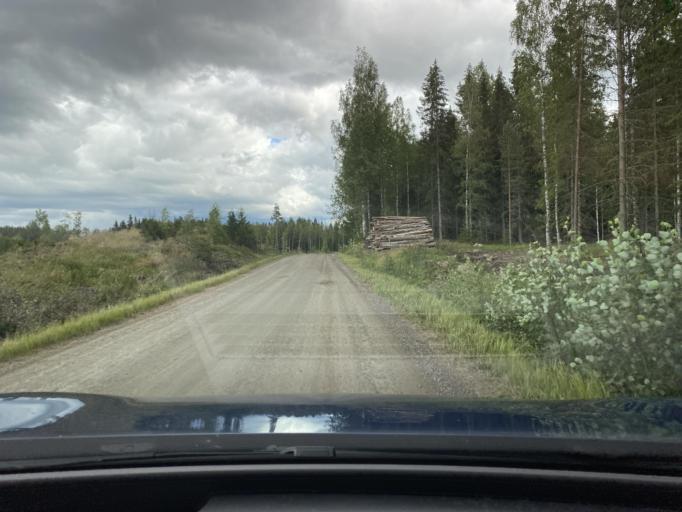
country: FI
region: Pirkanmaa
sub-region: Lounais-Pirkanmaa
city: Punkalaidun
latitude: 61.2253
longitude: 23.1571
